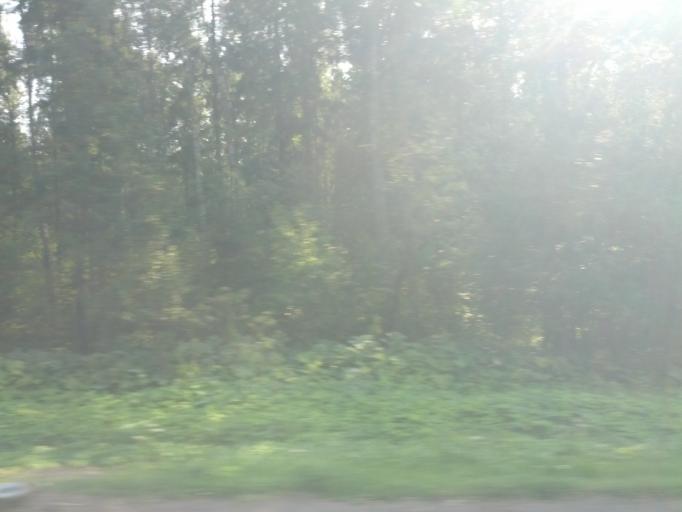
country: RU
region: Leningrad
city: Yanino Vtoroye
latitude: 59.8892
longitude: 30.5819
